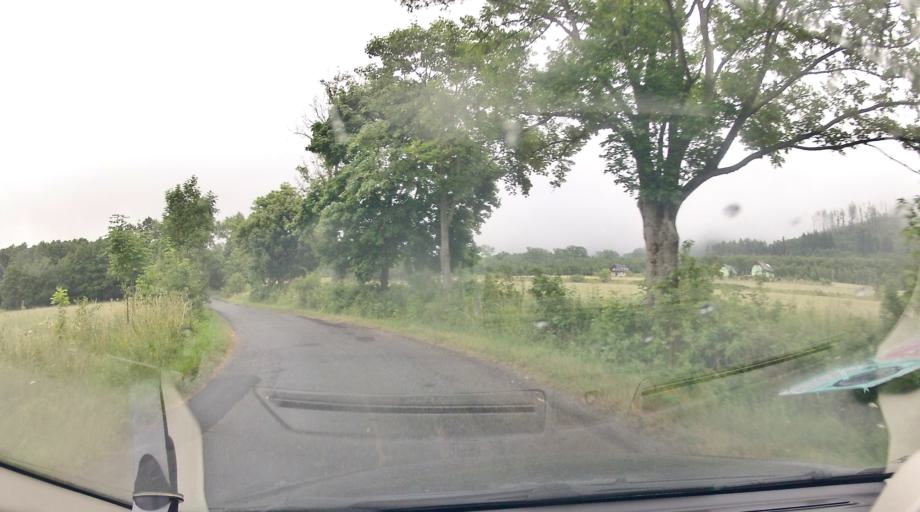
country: PL
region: Lower Silesian Voivodeship
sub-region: Powiat klodzki
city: Miedzylesie
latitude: 50.1895
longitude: 16.7347
